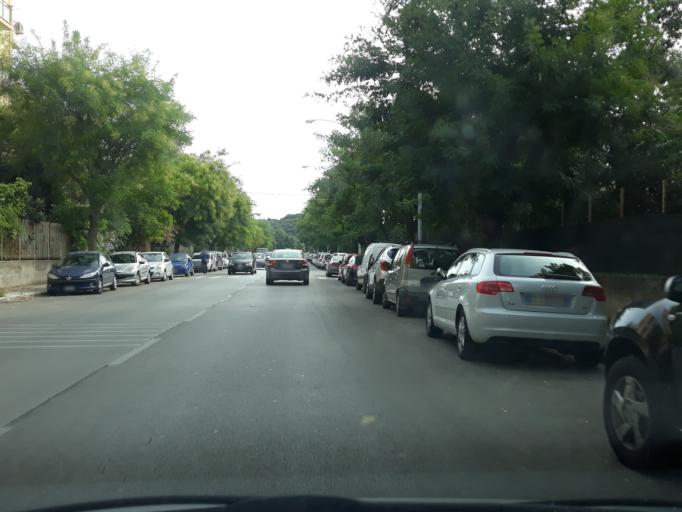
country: IT
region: Sicily
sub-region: Palermo
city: Palermo
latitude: 38.1012
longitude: 13.3278
